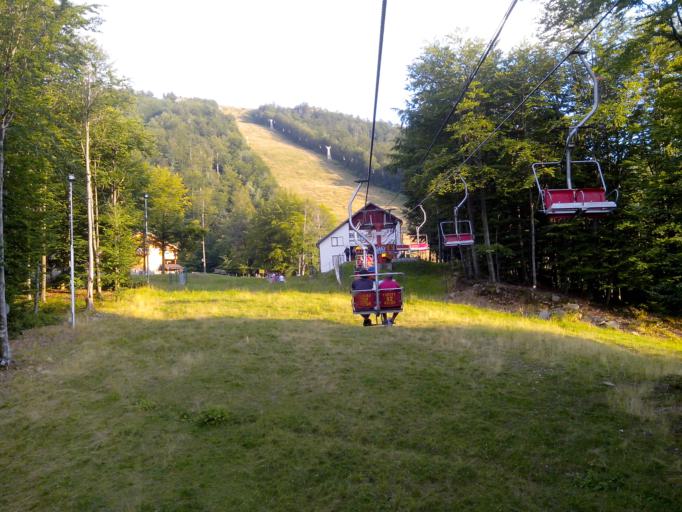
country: RO
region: Maramures
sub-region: Comuna Sisesti
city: Surdesti
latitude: 47.6661
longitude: 23.7821
